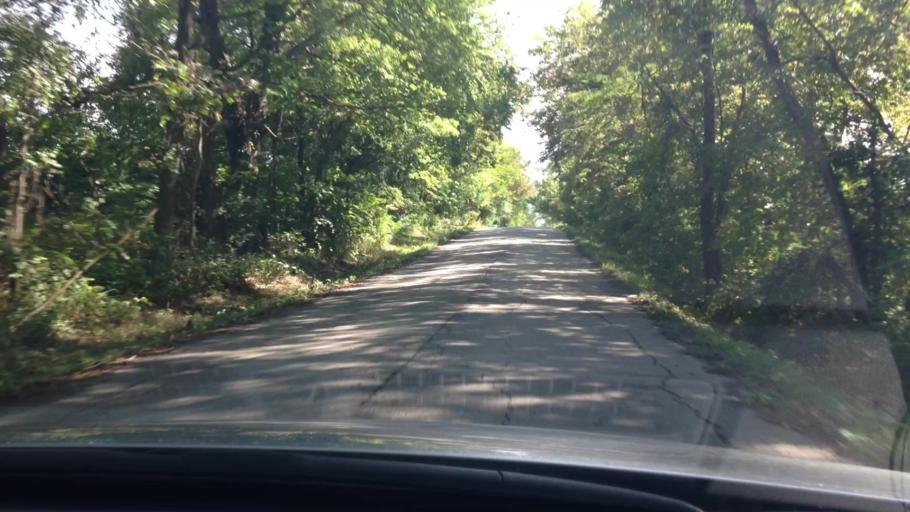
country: US
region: Missouri
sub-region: Platte County
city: Weatherby Lake
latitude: 39.3293
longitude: -94.6676
